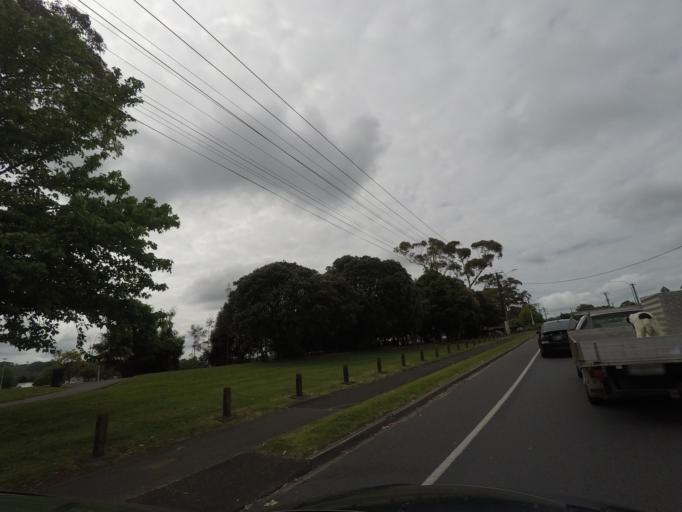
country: NZ
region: Auckland
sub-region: Auckland
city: Waitakere
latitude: -36.9059
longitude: 174.6270
